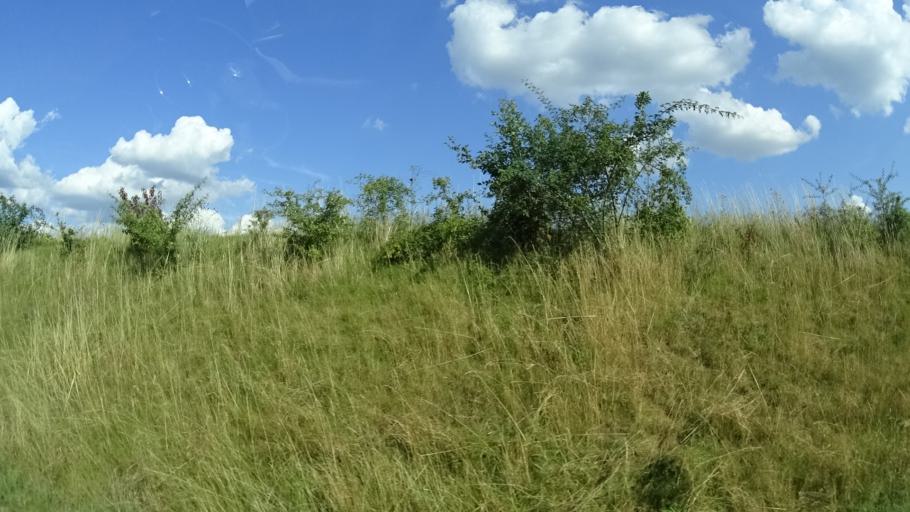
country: DE
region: Bavaria
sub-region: Regierungsbezirk Unterfranken
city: Oberelsbach
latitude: 50.4013
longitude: 10.0912
